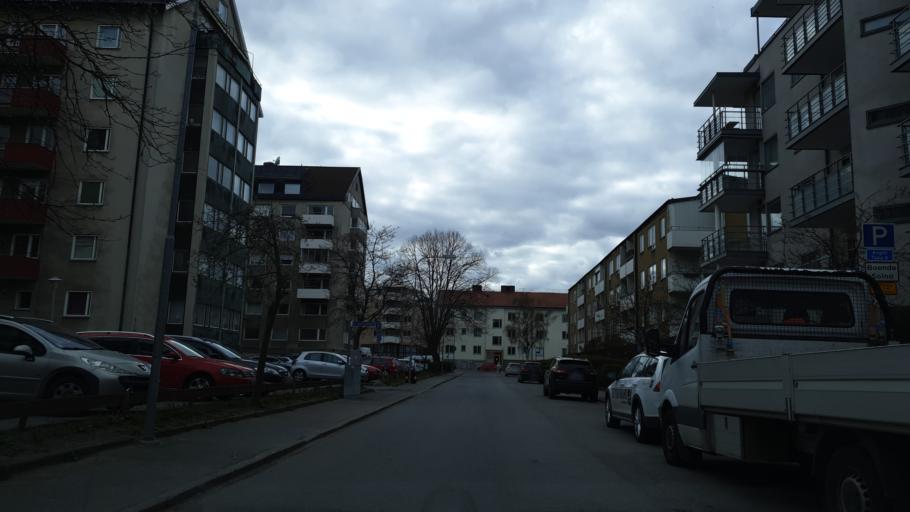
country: SE
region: Stockholm
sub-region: Solna Kommun
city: Solna
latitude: 59.3542
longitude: 18.0026
